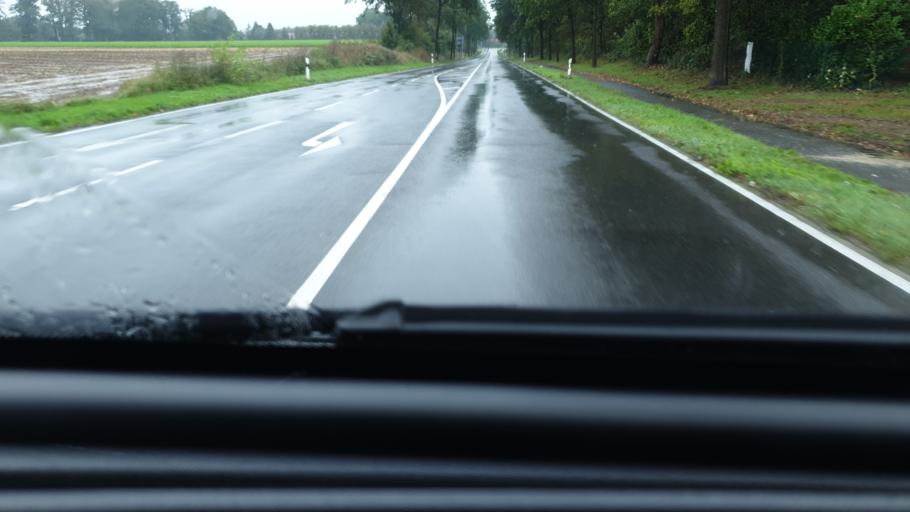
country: DE
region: North Rhine-Westphalia
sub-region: Regierungsbezirk Dusseldorf
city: Schwalmtal
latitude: 51.2147
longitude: 6.2869
